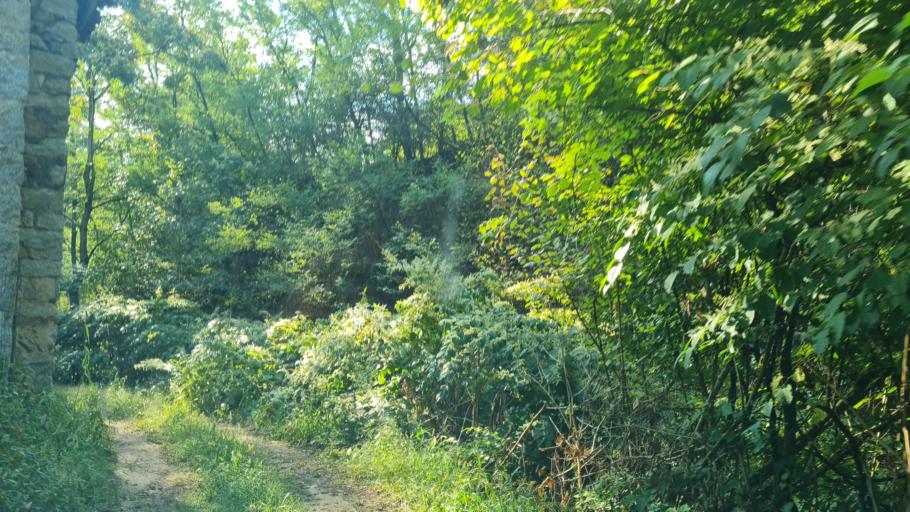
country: IT
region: Piedmont
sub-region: Provincia di Biella
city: Quaregna
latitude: 45.5882
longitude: 8.1643
